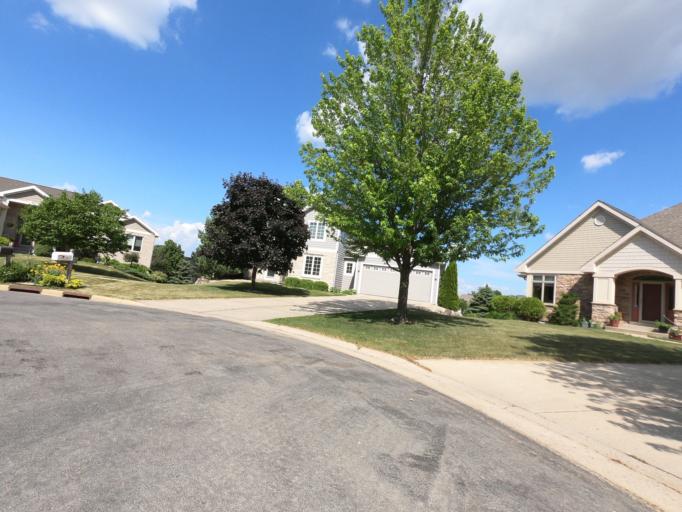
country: US
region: Wisconsin
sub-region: Dane County
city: Middleton
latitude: 43.0779
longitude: -89.5534
